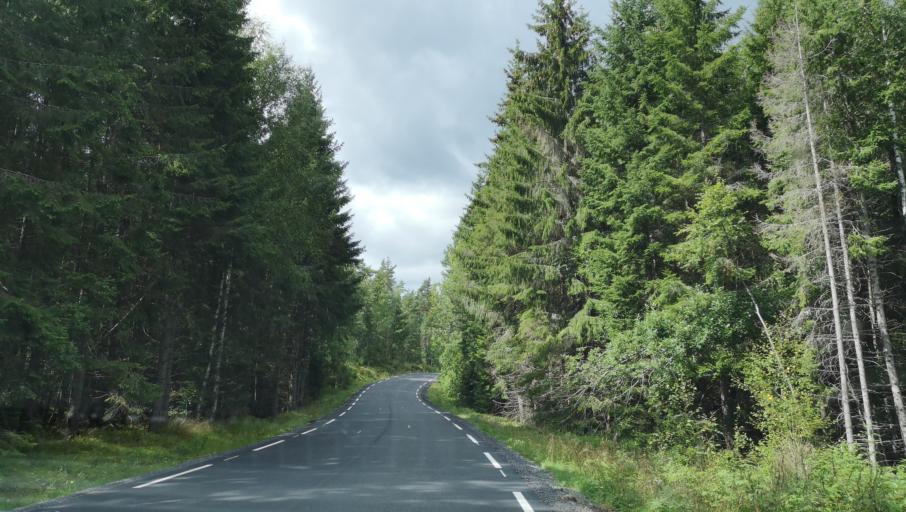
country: NO
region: Ostfold
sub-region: Hobol
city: Tomter
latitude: 59.6795
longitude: 10.9516
